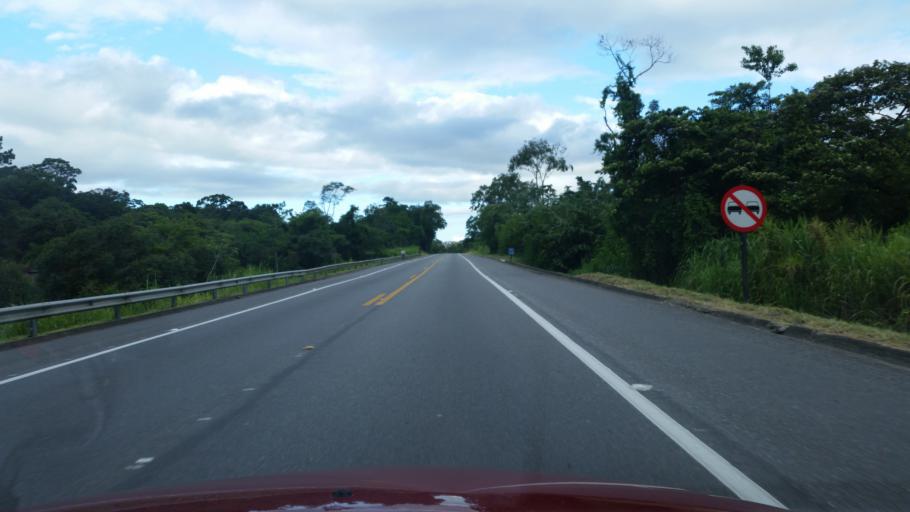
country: BR
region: Sao Paulo
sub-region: Miracatu
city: Miracatu
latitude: -24.2756
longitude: -47.2513
